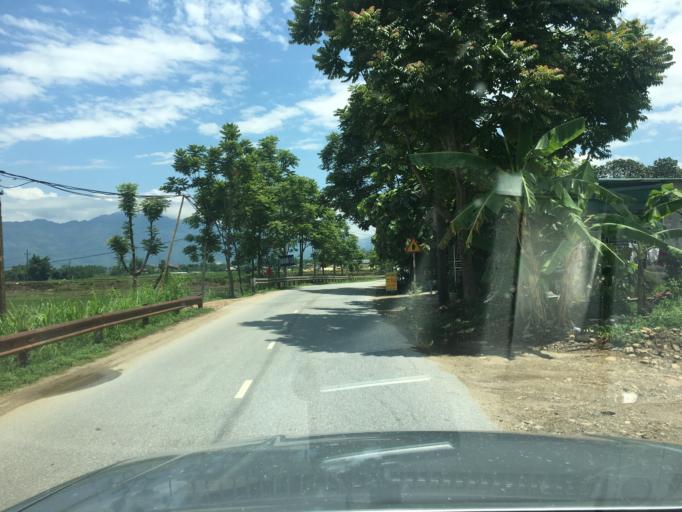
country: VN
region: Yen Bai
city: Son Thinh
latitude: 21.6216
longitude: 104.5092
